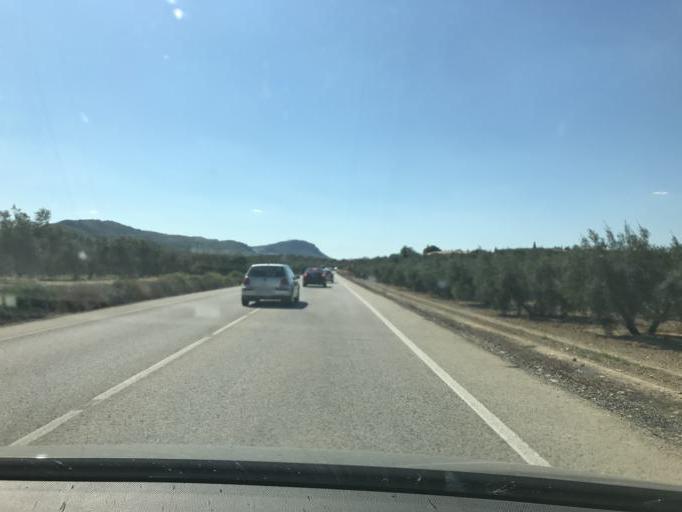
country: ES
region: Andalusia
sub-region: Province of Cordoba
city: Luque
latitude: 37.5646
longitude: -4.2207
